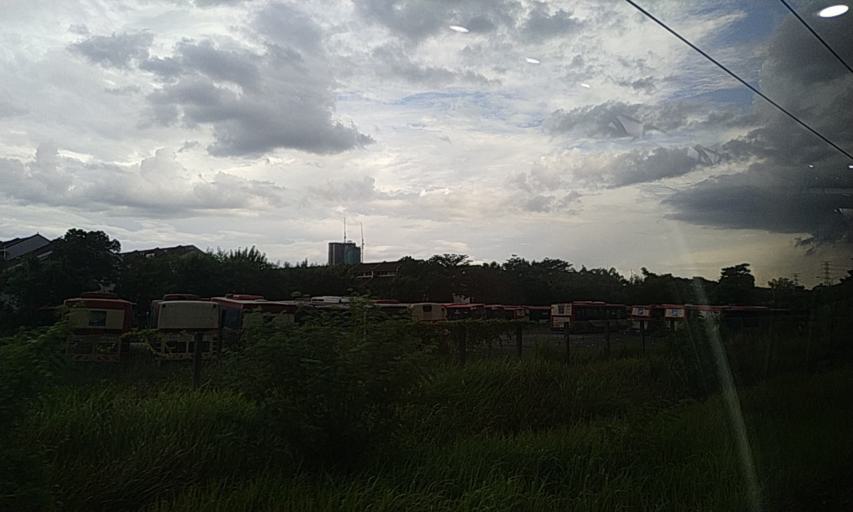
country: MY
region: Kuala Lumpur
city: Kuala Lumpur
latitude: 3.2183
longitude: 101.6724
